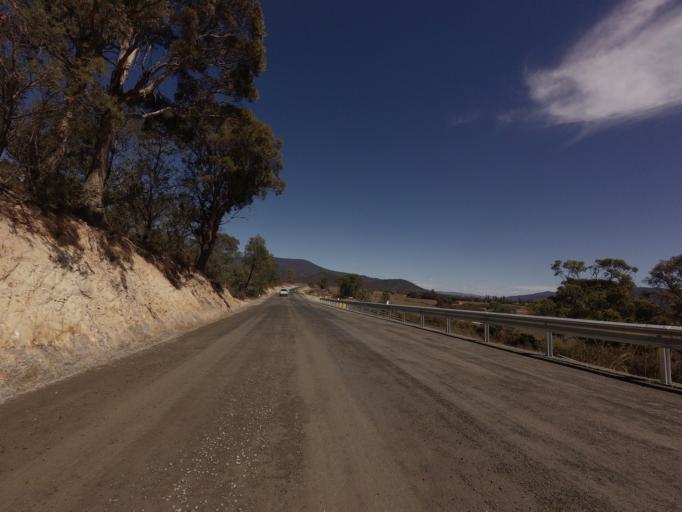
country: AU
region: Tasmania
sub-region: Break O'Day
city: St Helens
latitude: -41.6589
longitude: 147.9152
